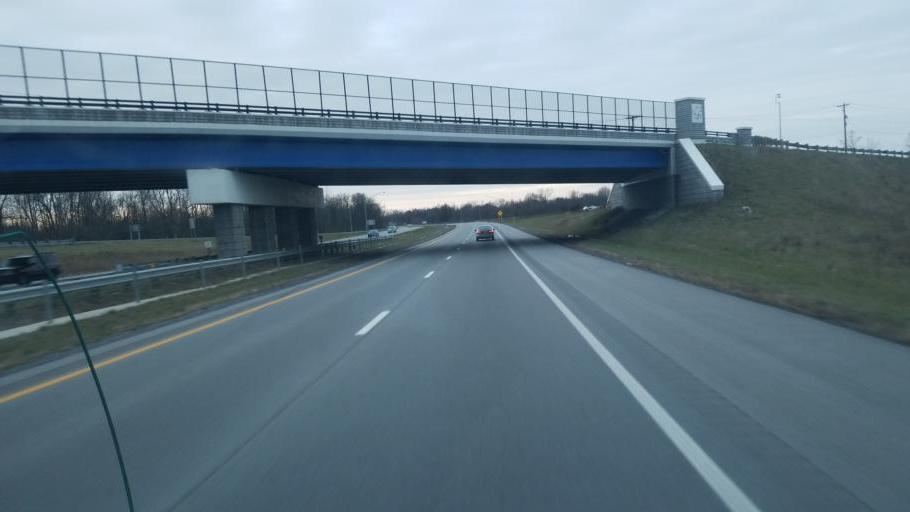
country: US
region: Ohio
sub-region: Allen County
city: Fort Shawnee
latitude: 40.6871
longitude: -84.1231
